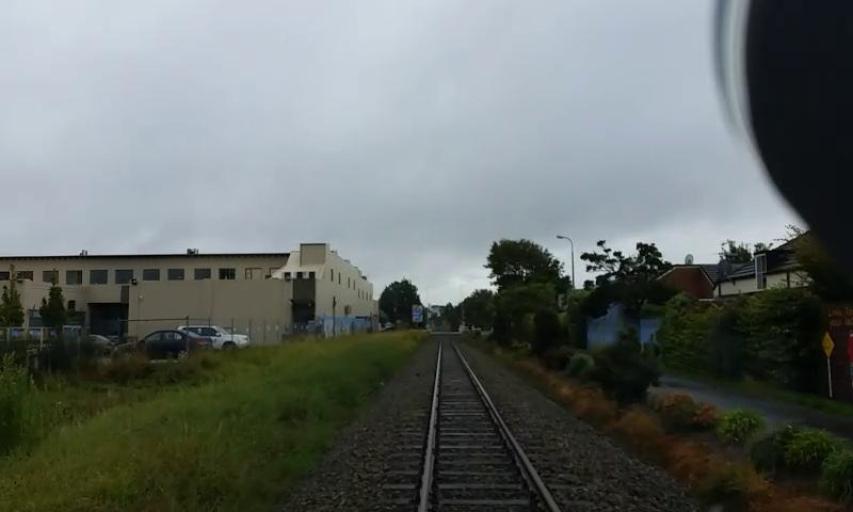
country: NZ
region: Canterbury
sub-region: Christchurch City
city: Christchurch
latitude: -43.5295
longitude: 172.6087
